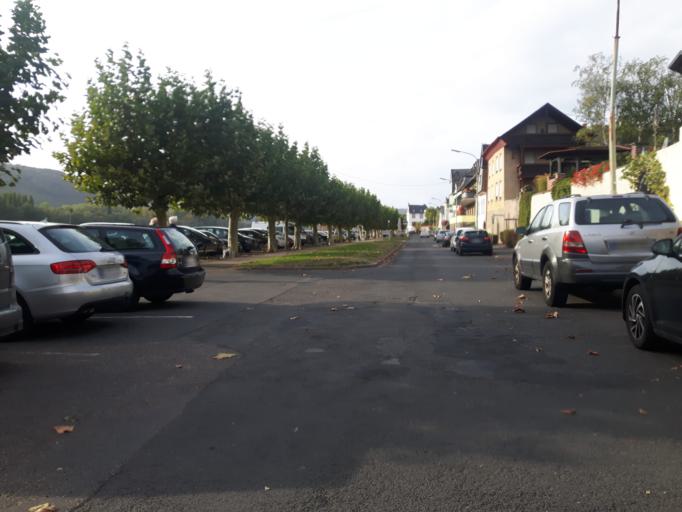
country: DE
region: Rheinland-Pfalz
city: Leutesdorf
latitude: 50.4485
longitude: 7.3882
